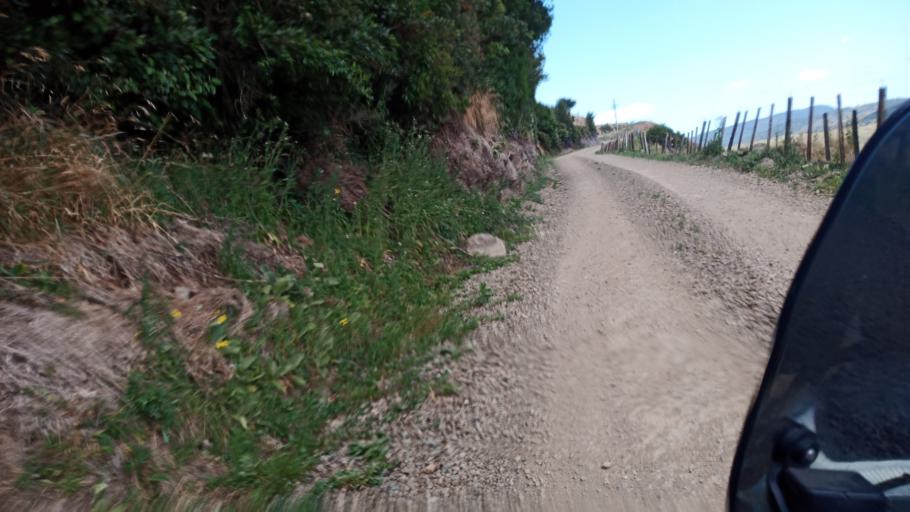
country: NZ
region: Gisborne
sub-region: Gisborne District
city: Gisborne
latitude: -38.4643
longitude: 177.5355
